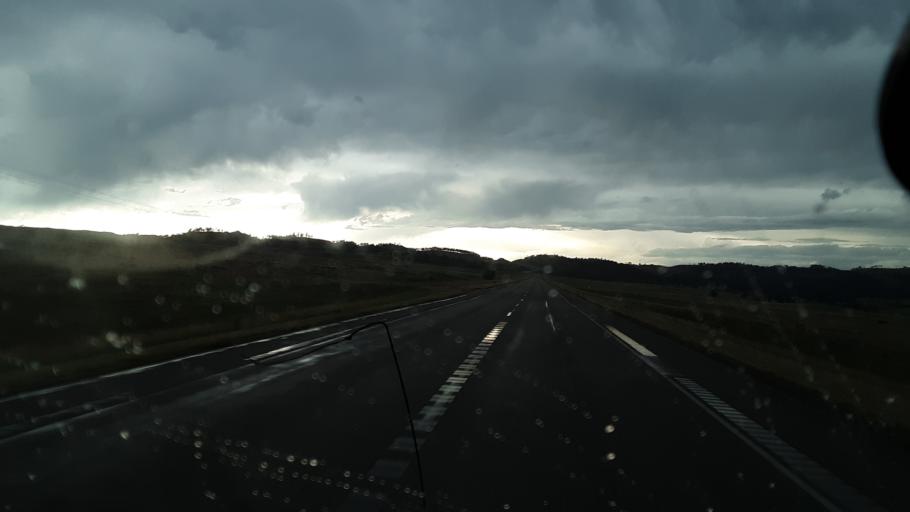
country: US
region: Montana
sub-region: Powder River County
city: Broadus
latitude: 45.5457
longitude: -105.8454
